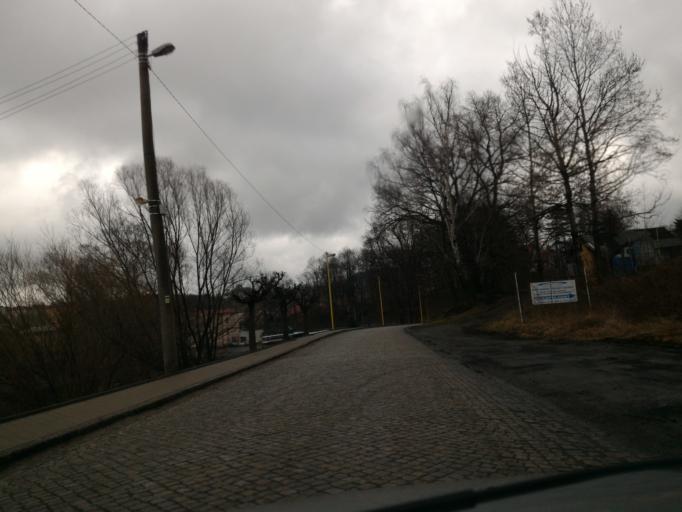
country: CZ
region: Liberecky
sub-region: Okres Liberec
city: Frydlant
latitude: 50.9190
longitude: 15.0767
